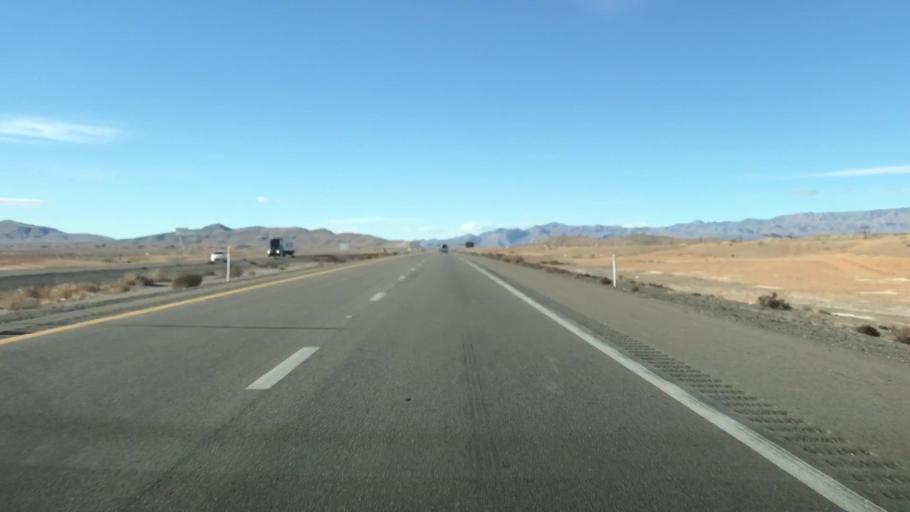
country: US
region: Nevada
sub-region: Clark County
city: Moapa Town
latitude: 36.4932
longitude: -114.7803
